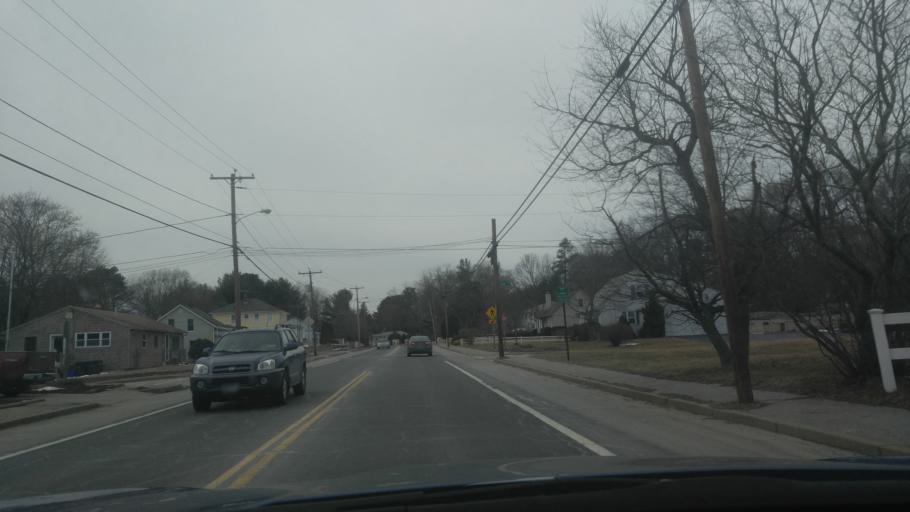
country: US
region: Rhode Island
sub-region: Kent County
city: West Warwick
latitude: 41.6963
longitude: -71.5751
